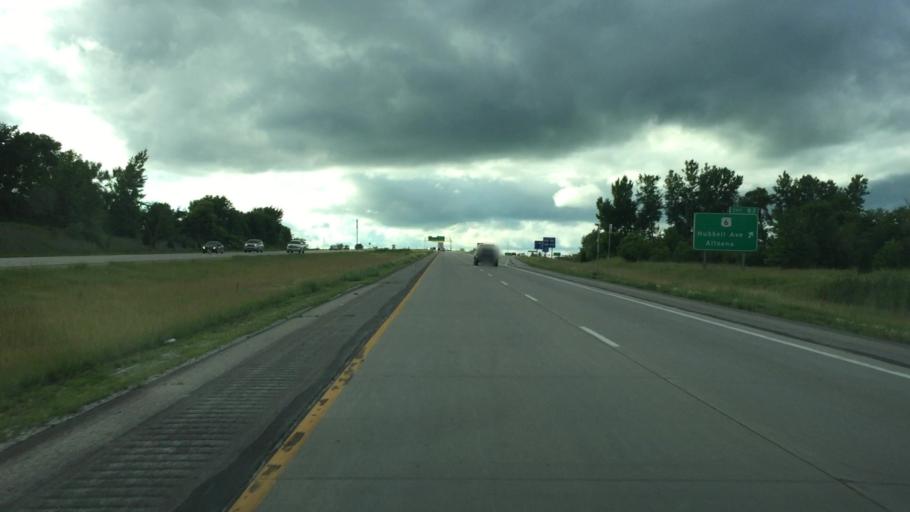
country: US
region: Iowa
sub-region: Polk County
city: Altoona
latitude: 41.6388
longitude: -93.5067
